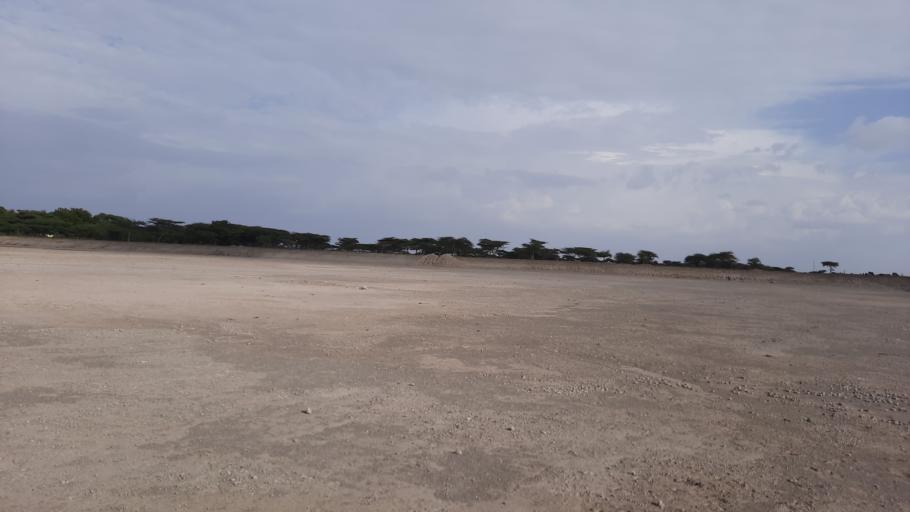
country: ET
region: Oromiya
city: Ziway
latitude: 7.6691
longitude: 38.6765
